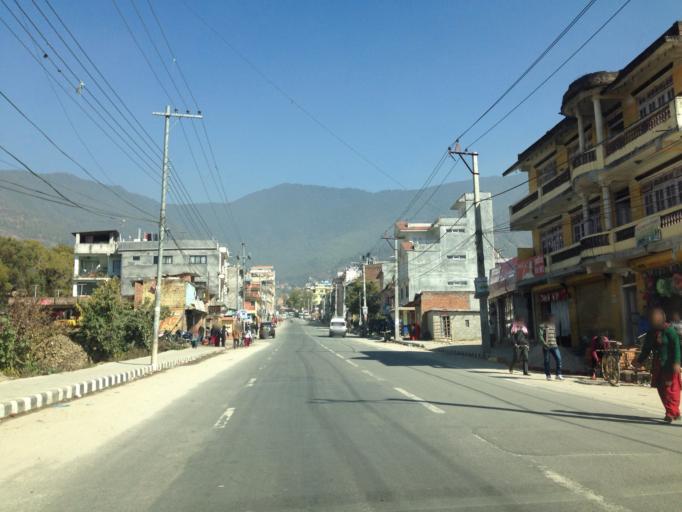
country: NP
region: Central Region
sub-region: Bagmati Zone
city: Kathmandu
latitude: 27.7732
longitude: 85.3600
